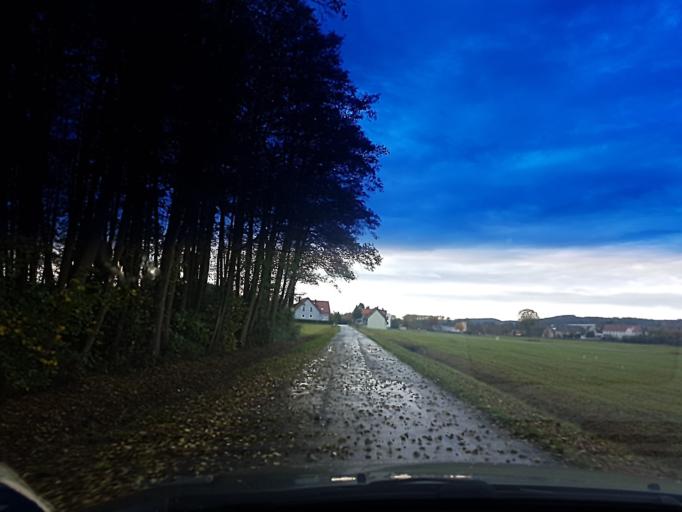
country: DE
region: Bavaria
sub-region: Regierungsbezirk Mittelfranken
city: Burghaslach
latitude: 49.7609
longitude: 10.5771
